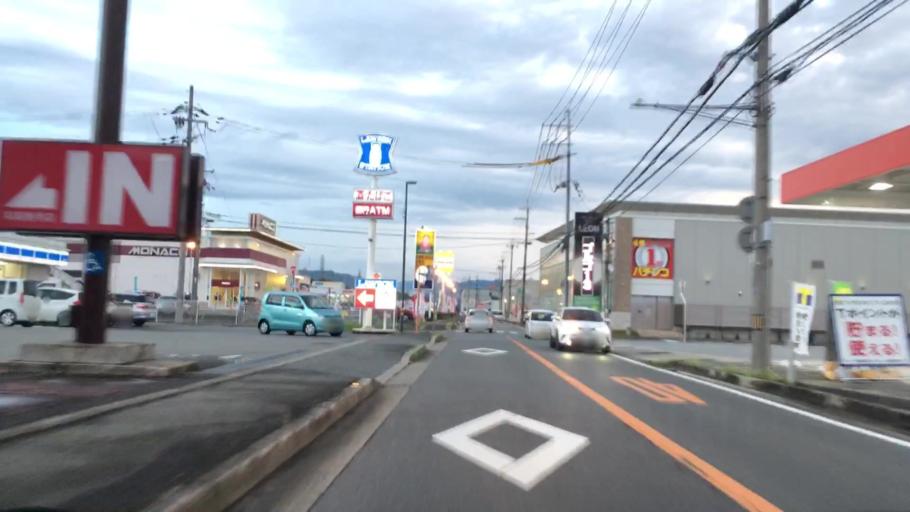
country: JP
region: Hyogo
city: Himeji
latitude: 34.9207
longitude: 134.7429
